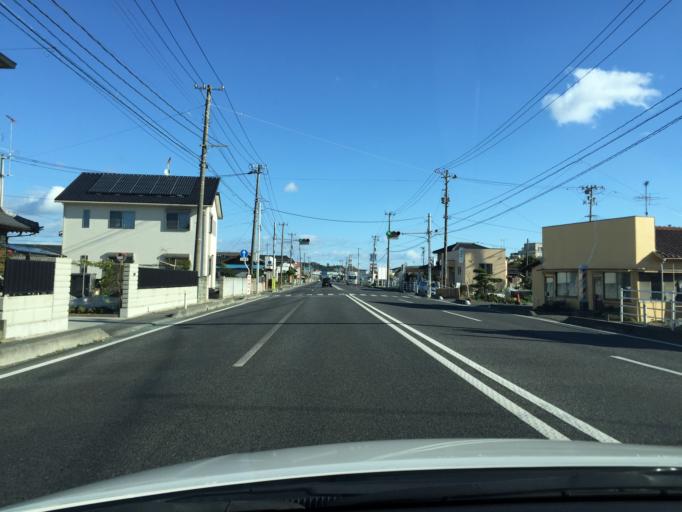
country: JP
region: Fukushima
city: Iwaki
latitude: 37.0984
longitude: 140.9815
